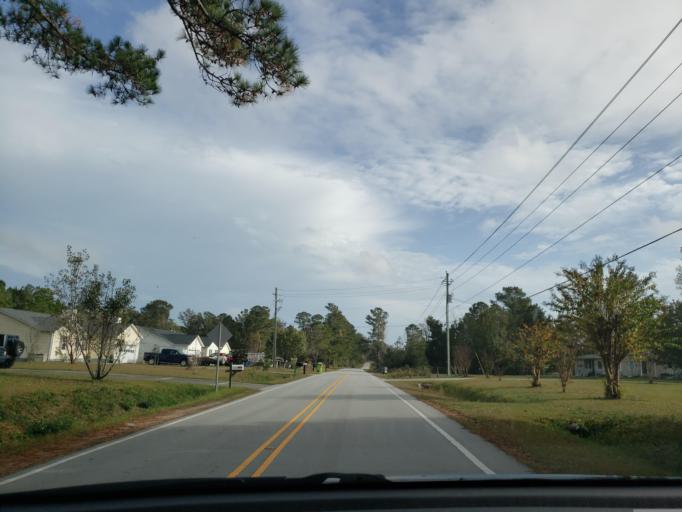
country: US
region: North Carolina
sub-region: Onslow County
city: Jacksonville
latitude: 34.6709
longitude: -77.4982
